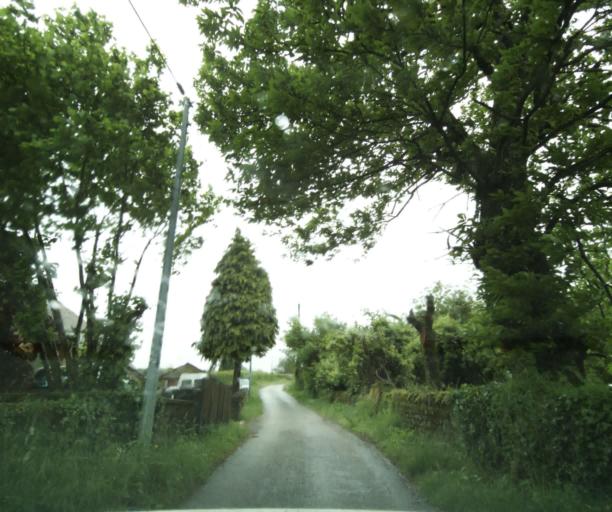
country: FR
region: Bourgogne
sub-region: Departement de Saone-et-Loire
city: Charolles
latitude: 46.4986
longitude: 4.3966
